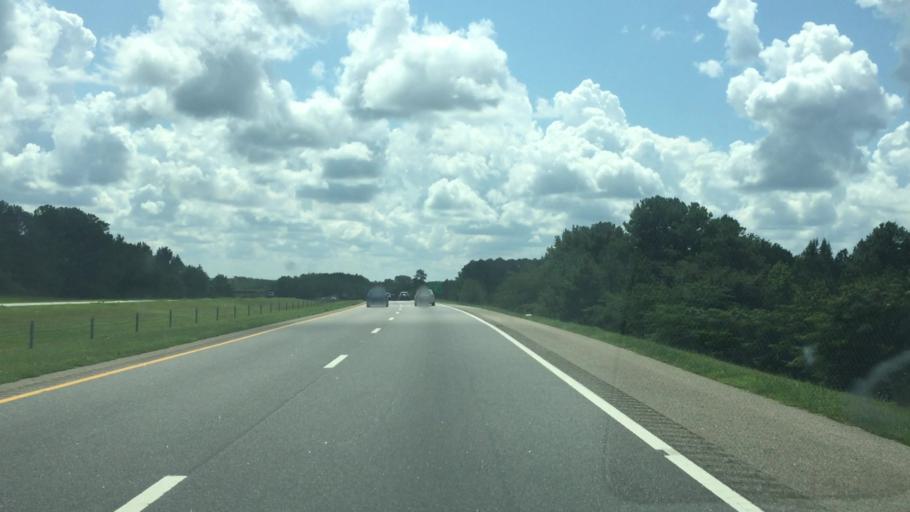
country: US
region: North Carolina
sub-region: Richmond County
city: Cordova
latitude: 34.9352
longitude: -79.8385
